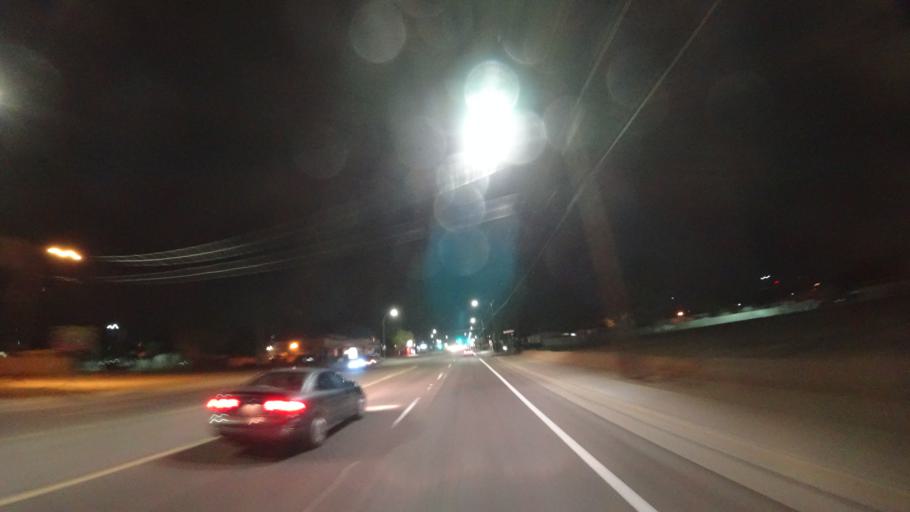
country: US
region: Arizona
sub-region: Maricopa County
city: Chandler
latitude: 33.3061
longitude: -111.8356
